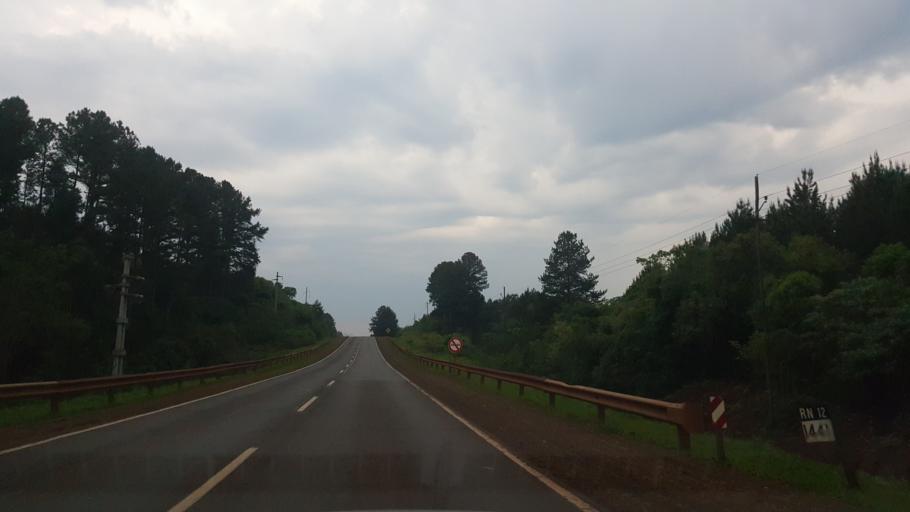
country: AR
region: Misiones
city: Jardin America
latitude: -27.0249
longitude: -55.2079
